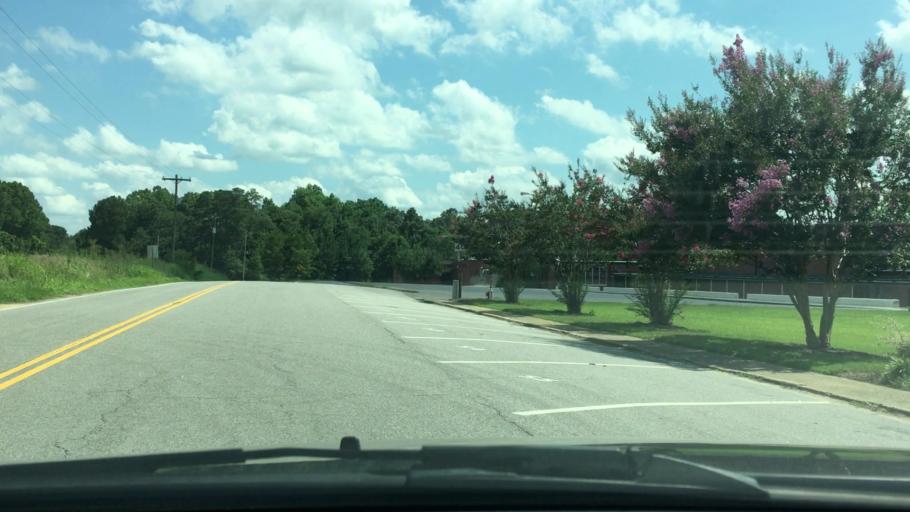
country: US
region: South Carolina
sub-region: Barnwell County
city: Williston
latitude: 33.6464
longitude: -81.3642
